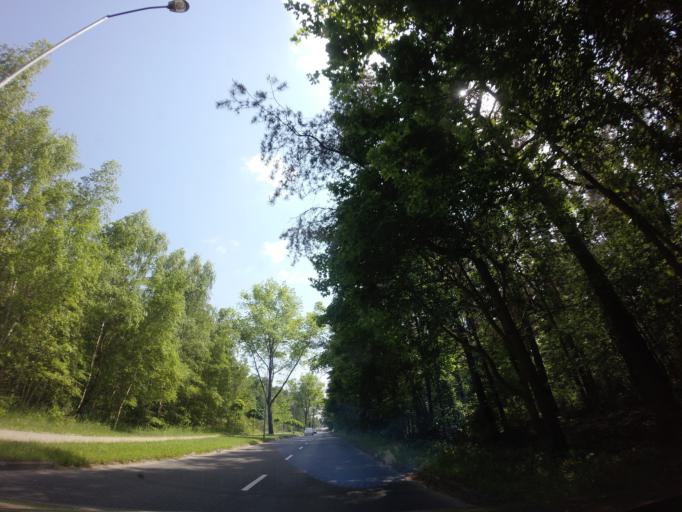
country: PL
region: West Pomeranian Voivodeship
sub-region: Powiat gryfinski
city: Stare Czarnowo
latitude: 53.3539
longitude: 14.7399
